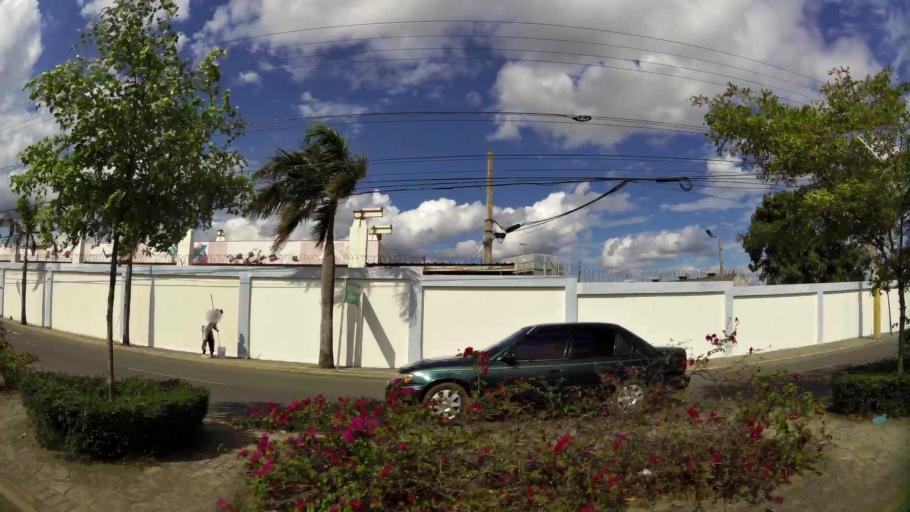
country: DO
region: La Vega
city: Concepcion de La Vega
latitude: 19.2289
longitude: -70.5267
